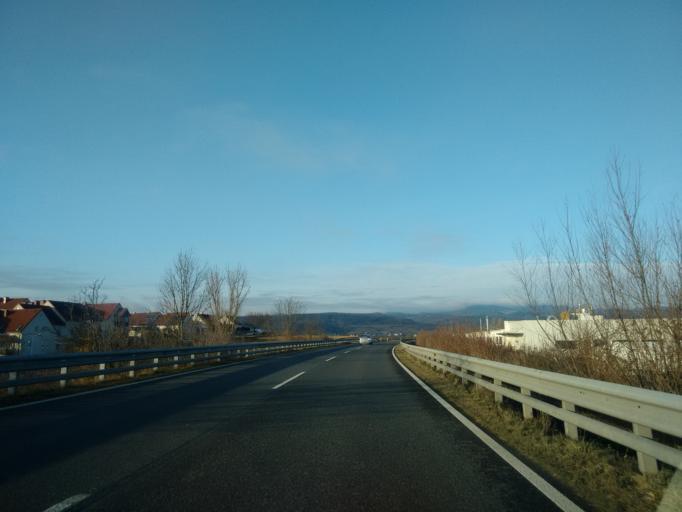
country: AT
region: Lower Austria
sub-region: Politischer Bezirk Melk
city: Melk
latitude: 48.2289
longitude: 15.3485
